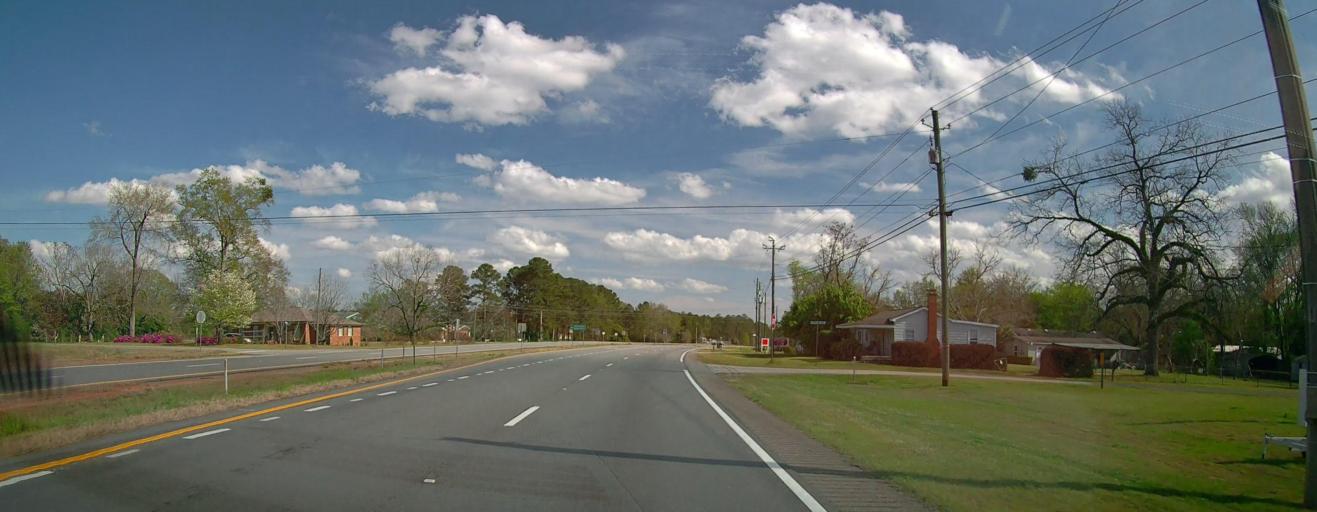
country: US
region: Georgia
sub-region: Baldwin County
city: Hardwick
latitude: 33.0201
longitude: -83.2298
